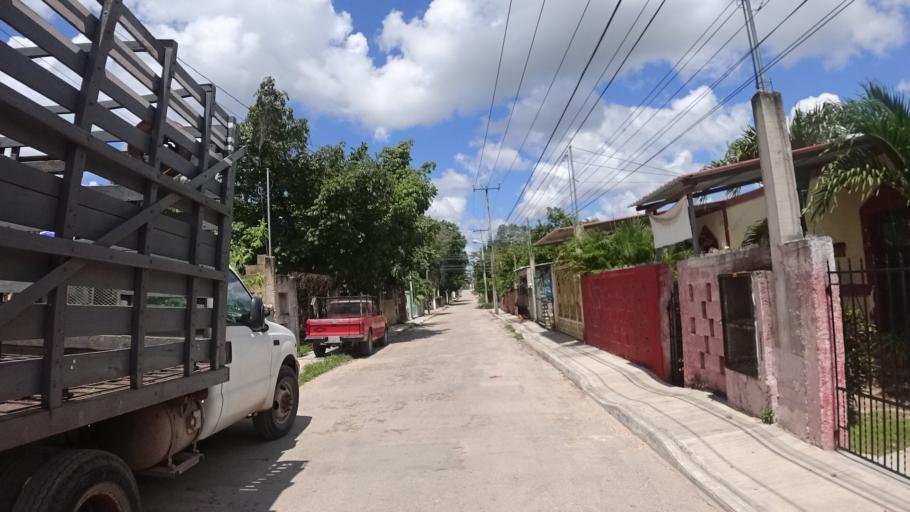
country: MX
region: Yucatan
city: Valladolid
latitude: 20.6838
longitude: -88.2131
